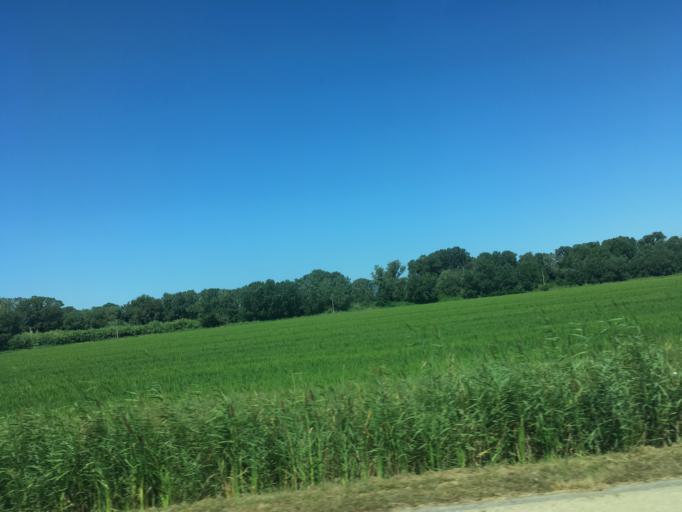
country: FR
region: Languedoc-Roussillon
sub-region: Departement du Gard
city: Saint-Gilles
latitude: 43.5951
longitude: 4.4703
